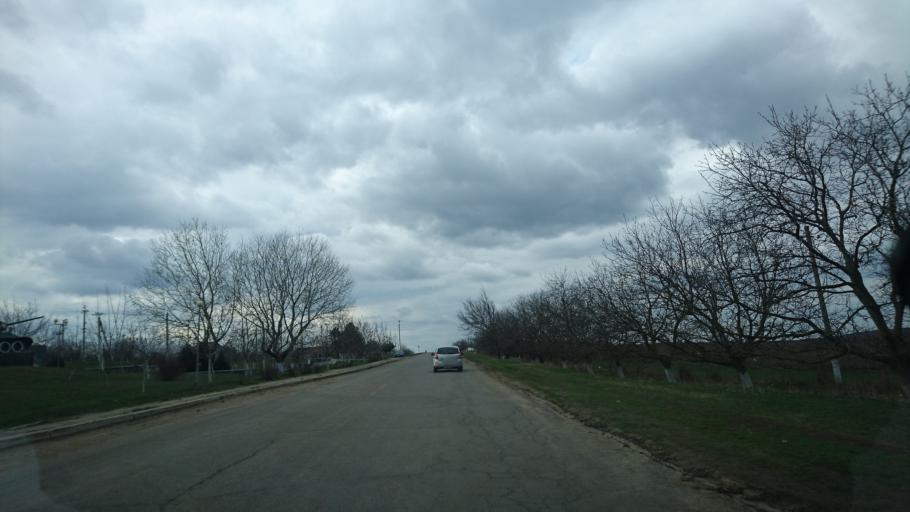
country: MD
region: Gagauzia
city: Comrat
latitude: 46.3050
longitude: 28.6264
